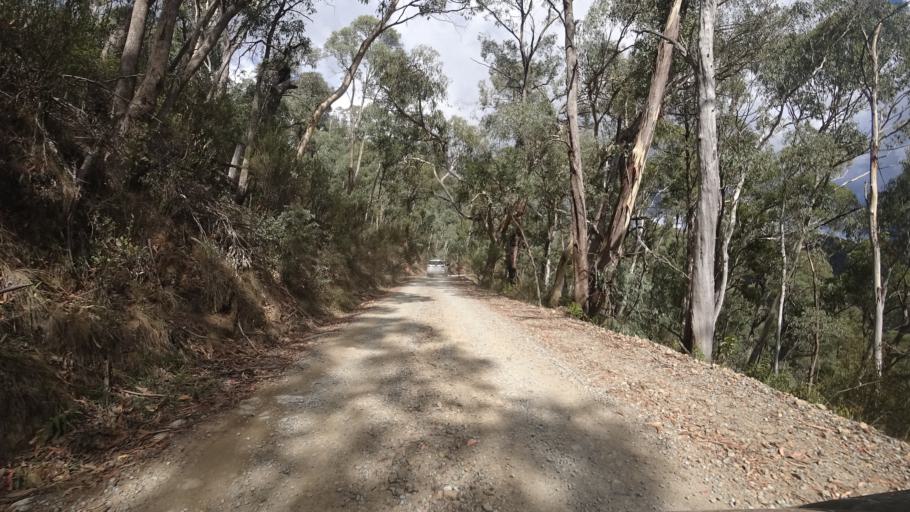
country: AU
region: New South Wales
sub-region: Tumut Shire
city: Tumut
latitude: -35.7288
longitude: 148.4874
